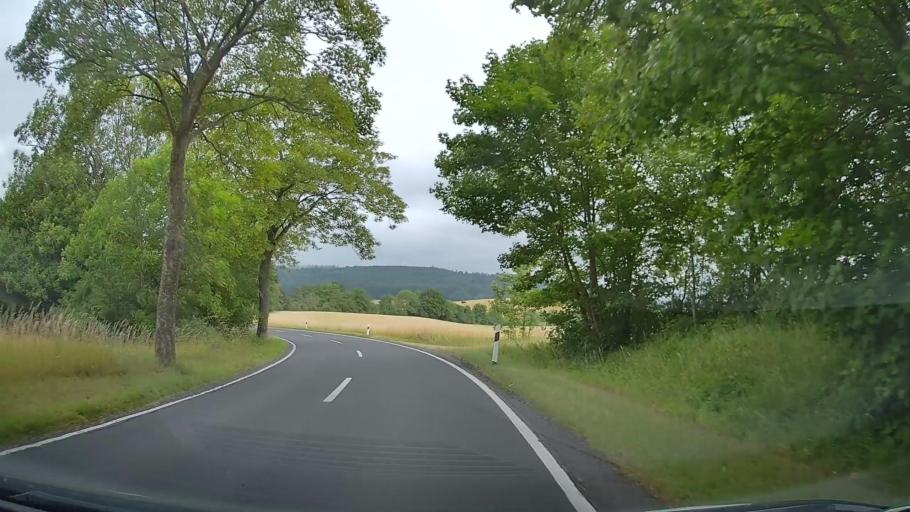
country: DE
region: Lower Saxony
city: Bad Pyrmont
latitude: 52.0044
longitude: 9.2079
